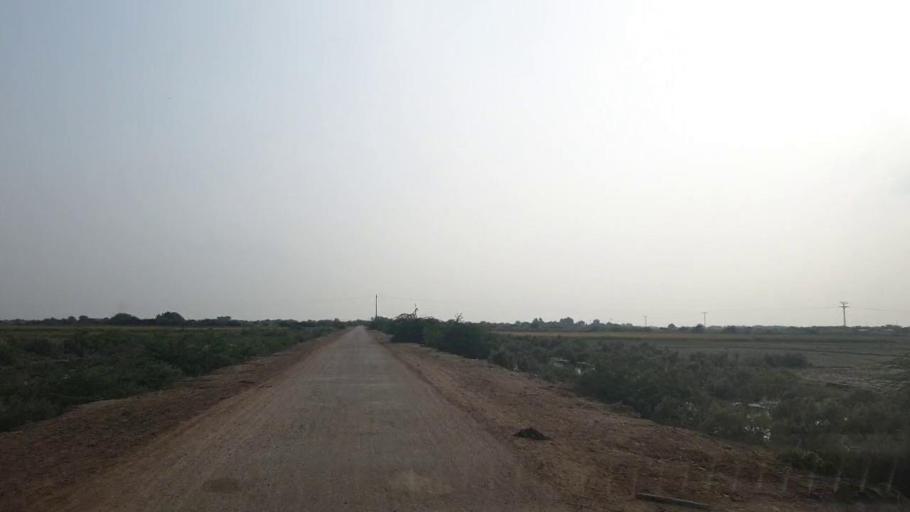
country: PK
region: Sindh
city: Badin
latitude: 24.6330
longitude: 68.6924
